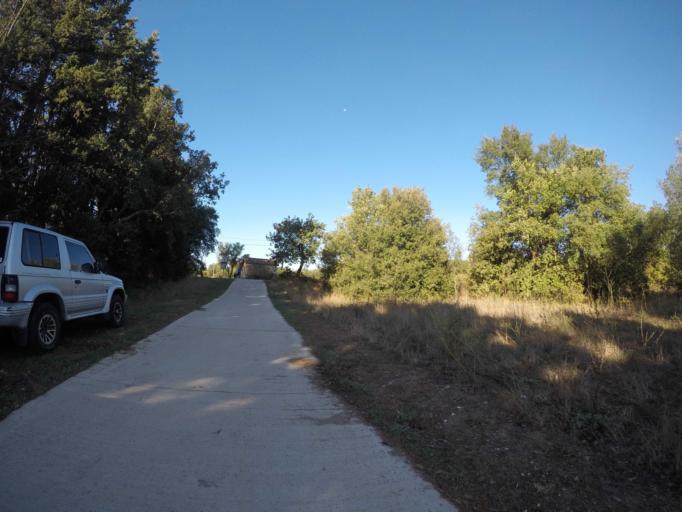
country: FR
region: Languedoc-Roussillon
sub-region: Departement des Pyrenees-Orientales
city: Sant Joan de Pladecorts
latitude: 42.5132
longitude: 2.7711
